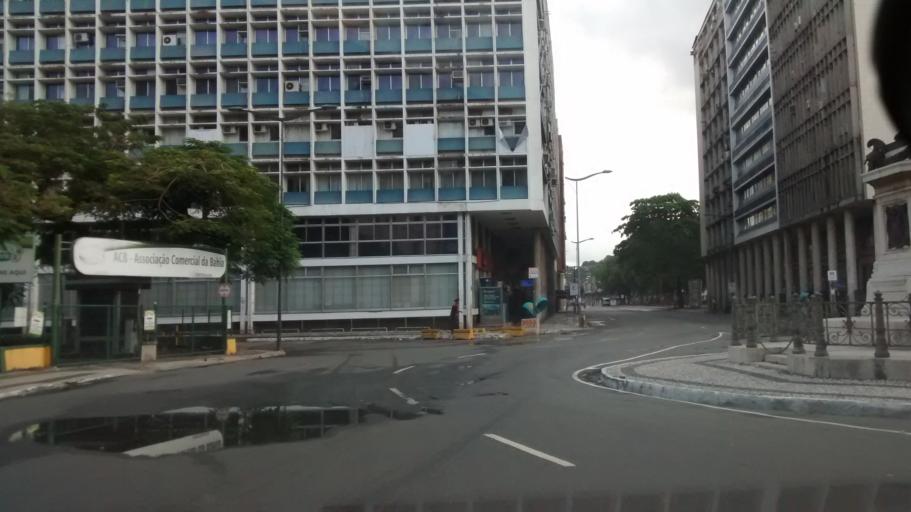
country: BR
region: Bahia
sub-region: Salvador
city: Salvador
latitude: -12.9701
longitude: -38.5112
